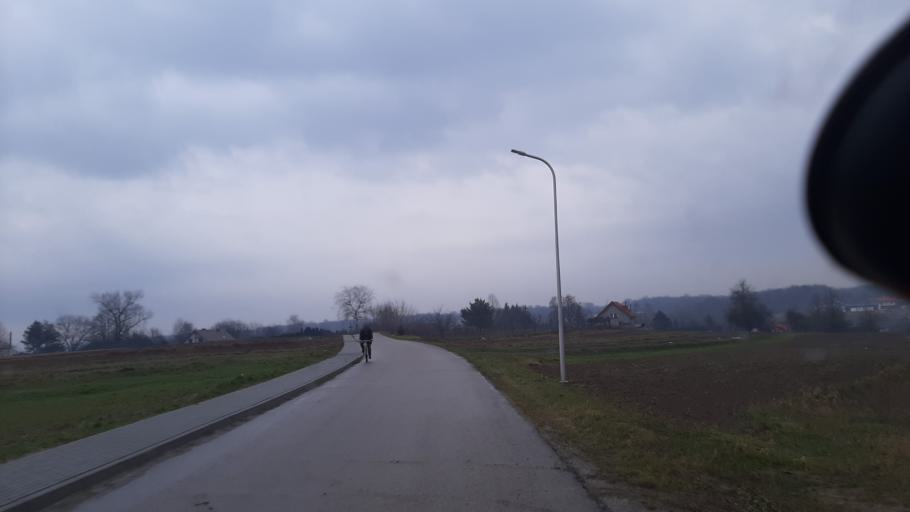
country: PL
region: Lublin Voivodeship
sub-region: Powiat lubelski
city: Lublin
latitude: 51.3182
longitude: 22.5780
